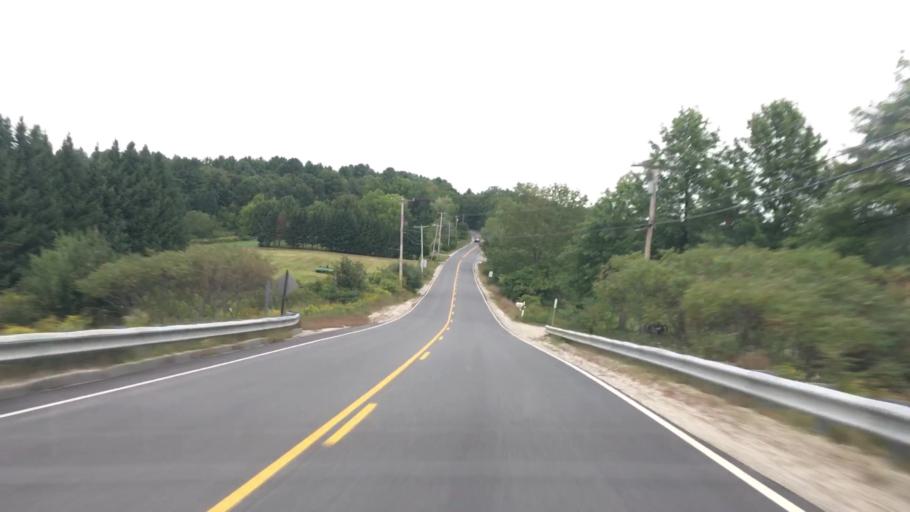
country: US
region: Maine
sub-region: Cumberland County
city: New Gloucester
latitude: 43.9184
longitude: -70.2498
